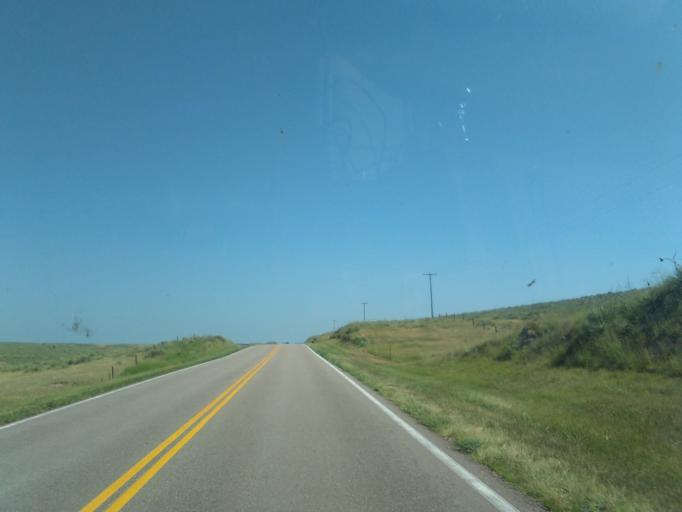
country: US
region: Nebraska
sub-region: Dundy County
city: Benkelman
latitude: 39.8776
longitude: -101.5411
